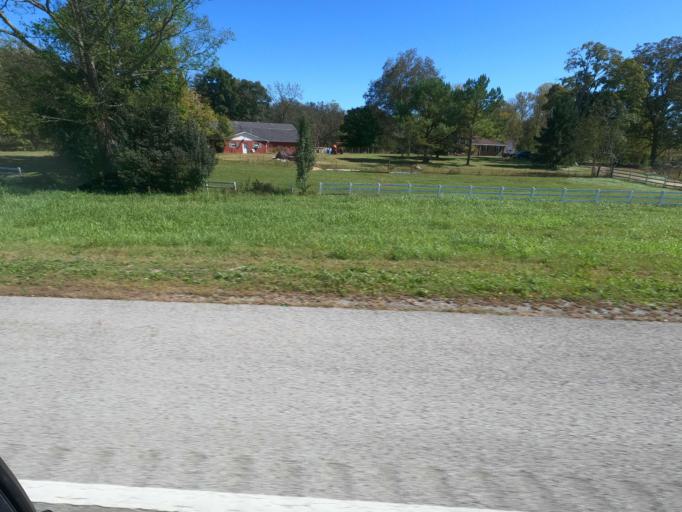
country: US
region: Tennessee
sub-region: Maury County
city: Mount Pleasant
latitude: 35.5013
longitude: -87.2320
